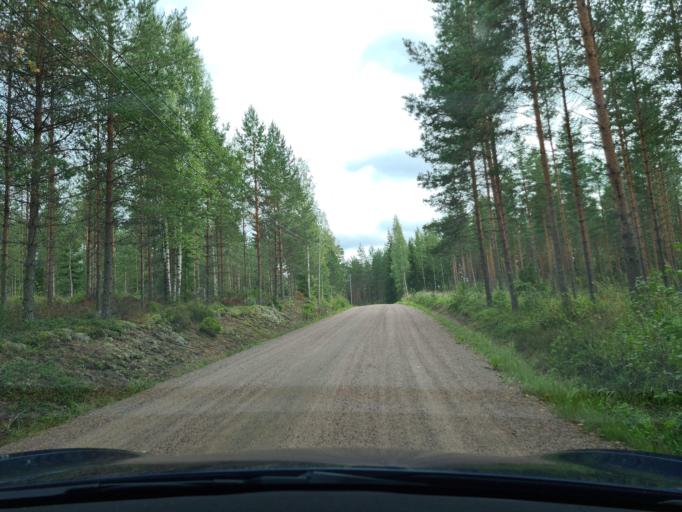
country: FI
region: Uusimaa
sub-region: Helsinki
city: Vihti
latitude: 60.4193
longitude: 24.4813
